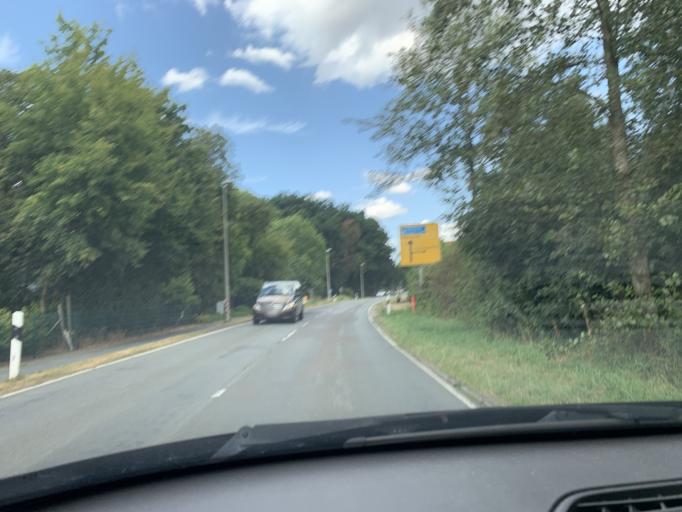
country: DE
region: Lower Saxony
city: Bad Zwischenahn
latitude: 53.1942
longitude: 8.0435
